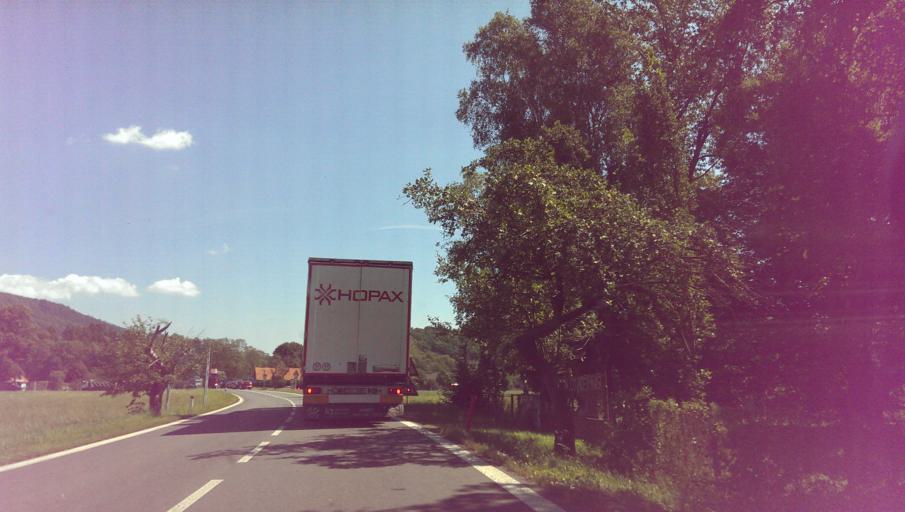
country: CZ
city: Lichnov (o. Novy Jicin)
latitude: 49.5981
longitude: 18.1862
